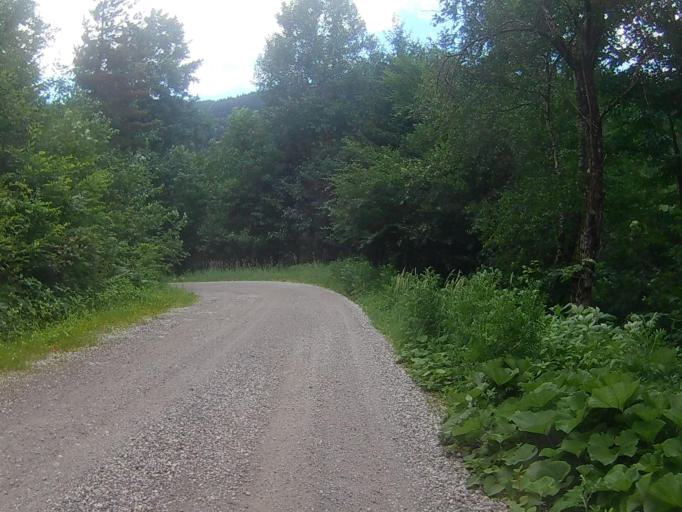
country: SI
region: Selnica ob Dravi
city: Selnica ob Dravi
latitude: 46.5241
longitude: 15.4668
